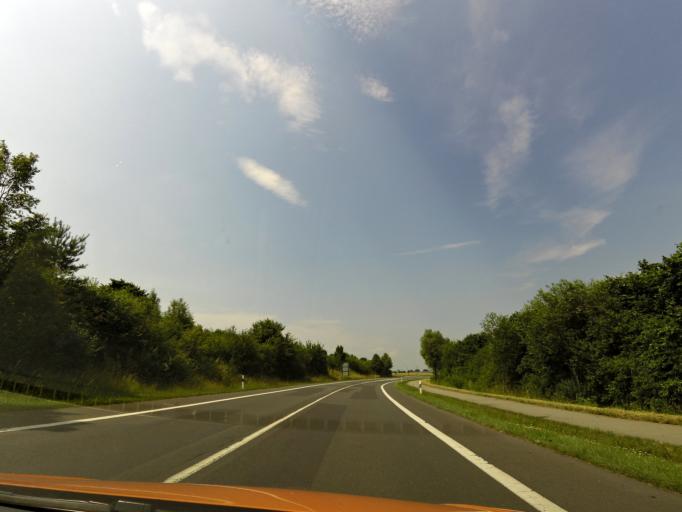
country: DE
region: Brandenburg
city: Gerdshagen
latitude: 53.2126
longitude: 12.2066
